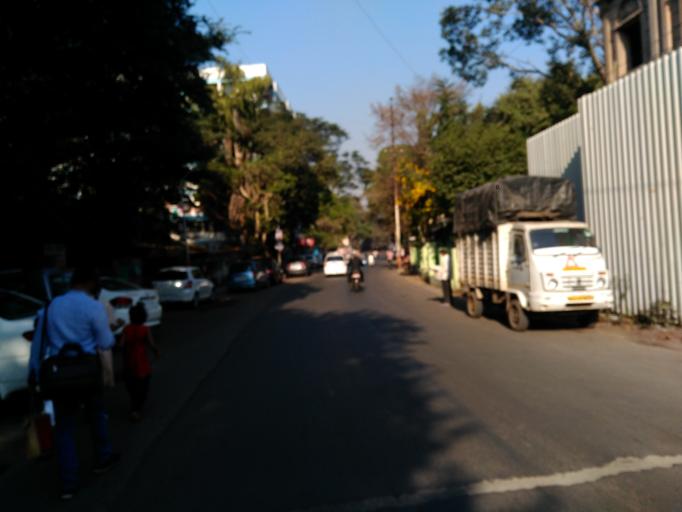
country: IN
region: Maharashtra
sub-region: Pune Division
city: Pune
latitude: 18.5156
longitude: 73.8753
